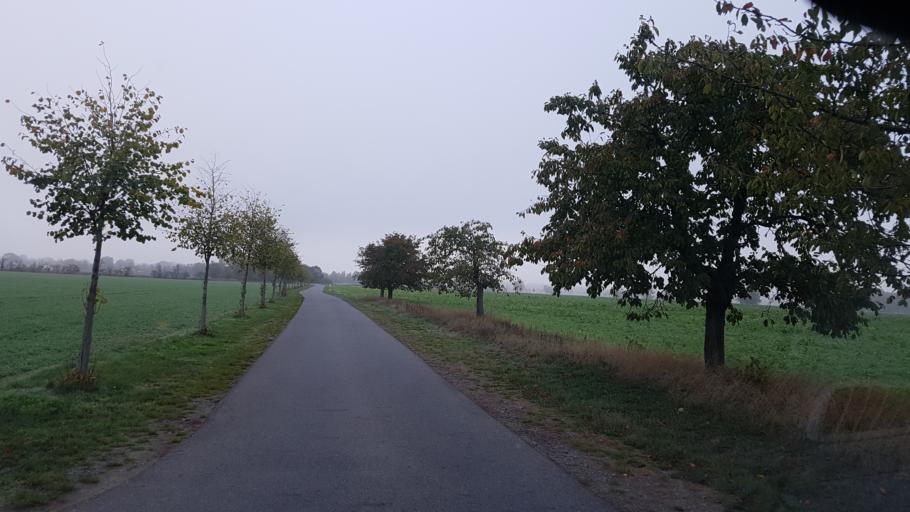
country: DE
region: Brandenburg
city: Schonewalde
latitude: 51.6768
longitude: 13.6227
